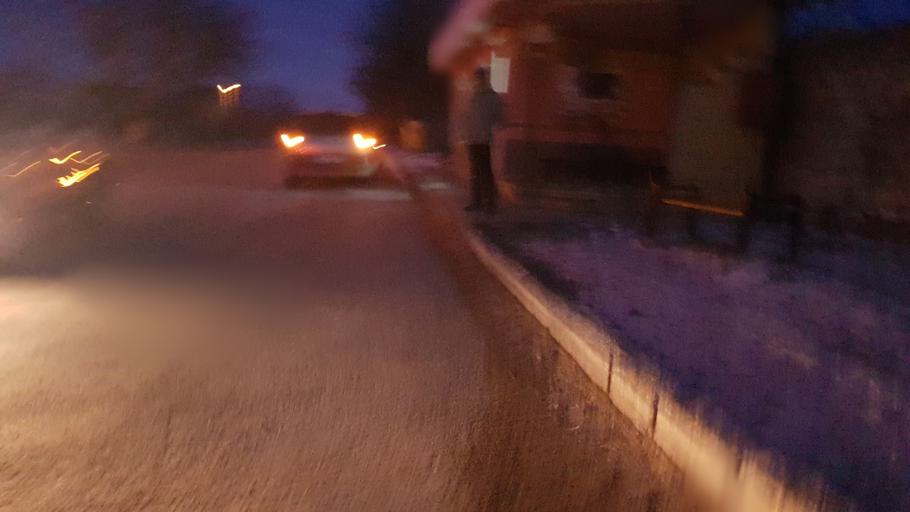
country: MD
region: Chisinau
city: Cricova
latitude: 47.1454
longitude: 28.8547
